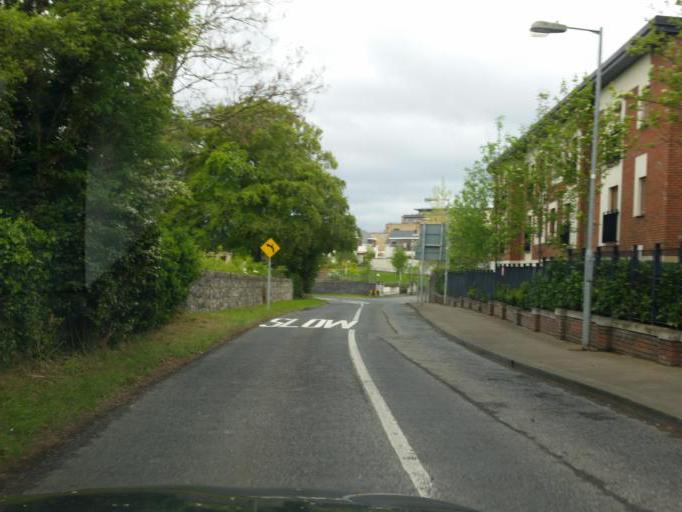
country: IE
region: Leinster
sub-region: Dublin City
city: Finglas
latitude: 53.3784
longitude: -6.3250
